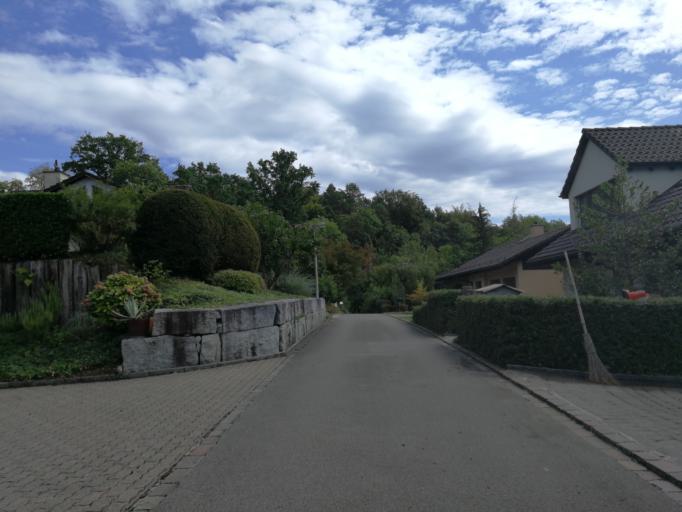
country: CH
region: Zurich
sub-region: Bezirk Meilen
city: Feldmeilen
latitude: 47.2849
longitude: 8.6247
